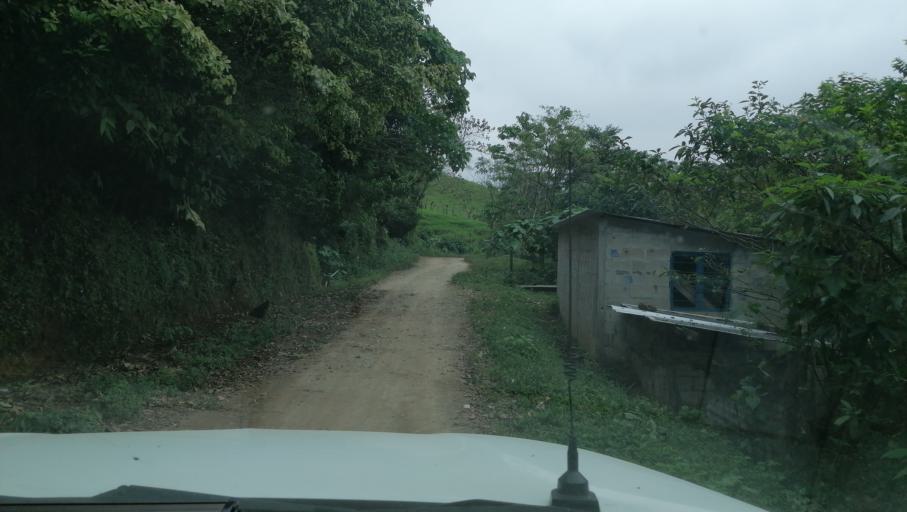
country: MX
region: Chiapas
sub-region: Francisco Leon
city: San Miguel la Sardina
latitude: 17.3438
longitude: -93.3108
